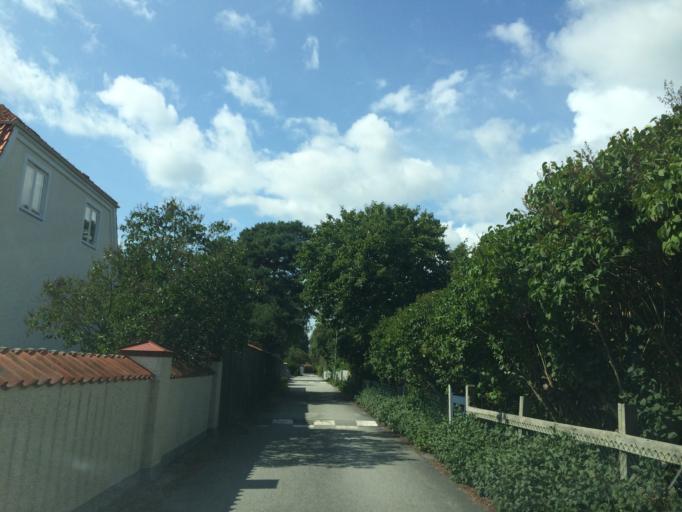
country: SE
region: Skane
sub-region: Vellinge Kommun
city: Skanor med Falsterbo
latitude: 55.3971
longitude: 12.8355
